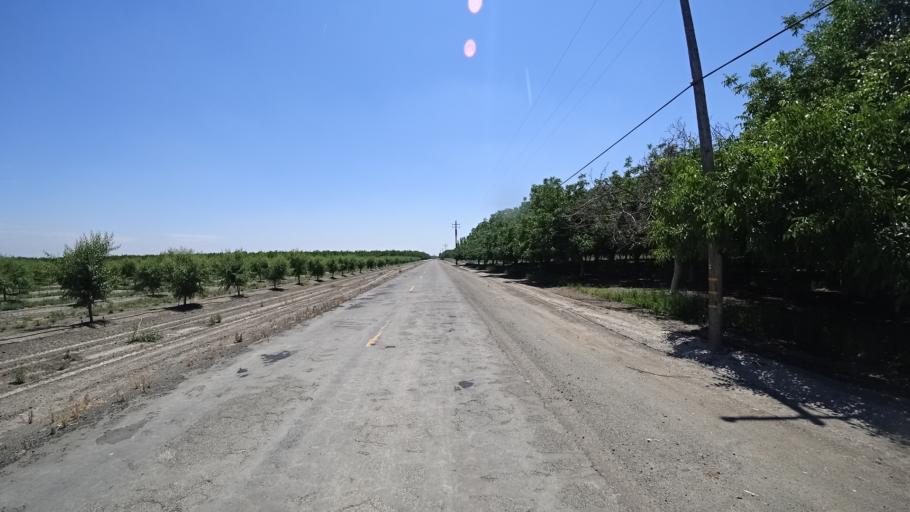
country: US
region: California
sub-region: Kings County
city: Lucerne
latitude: 36.4077
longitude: -119.6189
